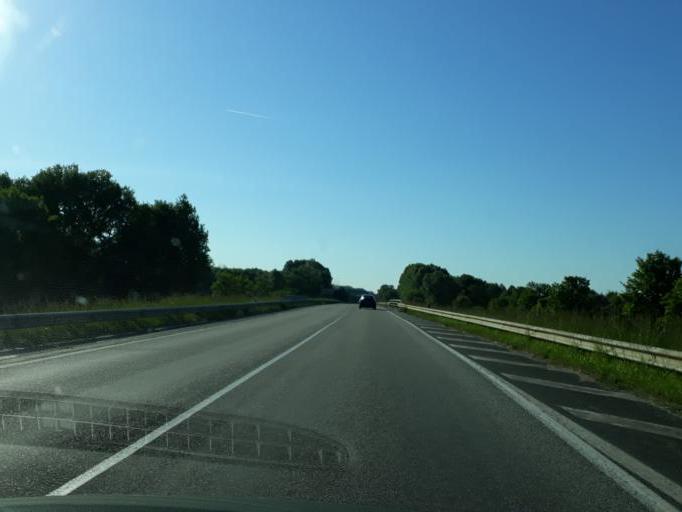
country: FR
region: Centre
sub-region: Departement du Loiret
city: Bonny-sur-Loire
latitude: 47.5469
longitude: 2.8526
